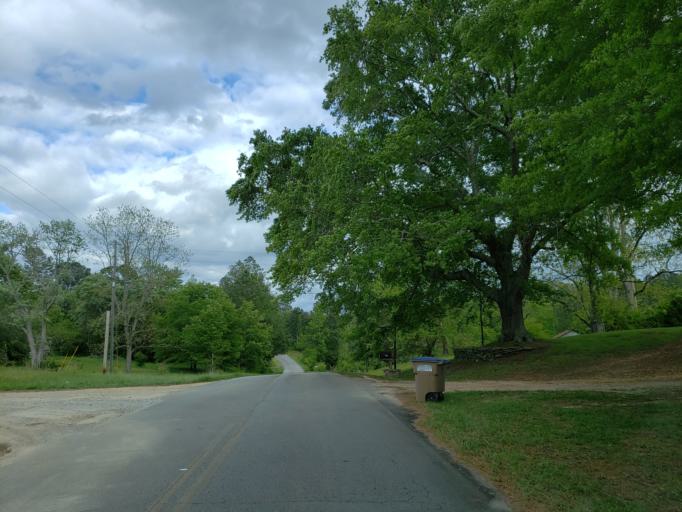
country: US
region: Georgia
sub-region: Haralson County
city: Tallapoosa
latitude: 33.7849
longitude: -85.3318
